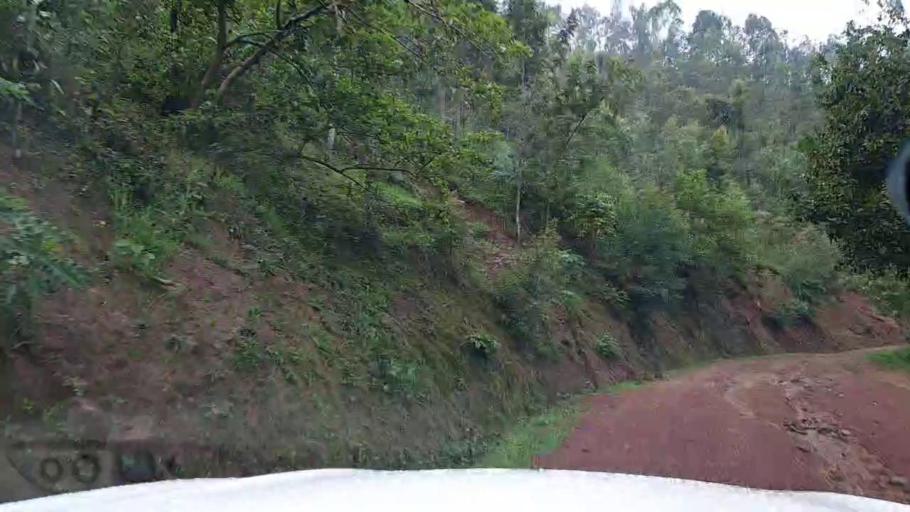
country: RW
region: Northern Province
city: Byumba
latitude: -1.7231
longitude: 29.9171
